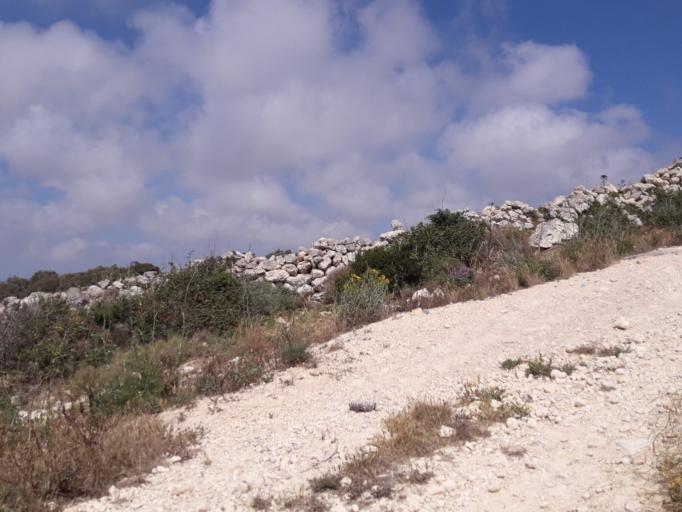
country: MT
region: Dingli
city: Dingli
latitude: 35.8660
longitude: 14.3622
